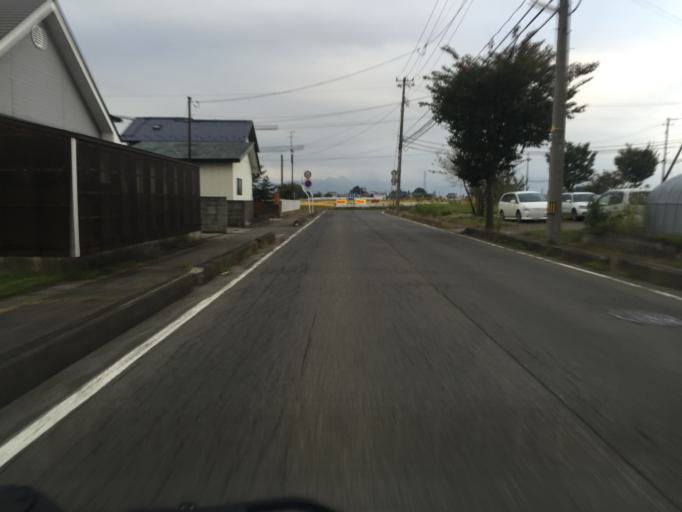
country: JP
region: Fukushima
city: Kitakata
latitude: 37.5110
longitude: 139.8775
